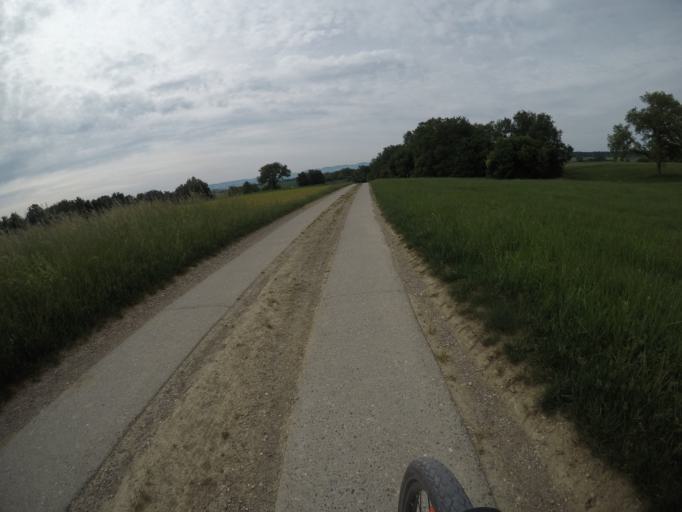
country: DE
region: Baden-Wuerttemberg
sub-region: Tuebingen Region
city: Pliezhausen
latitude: 48.5930
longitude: 9.1688
